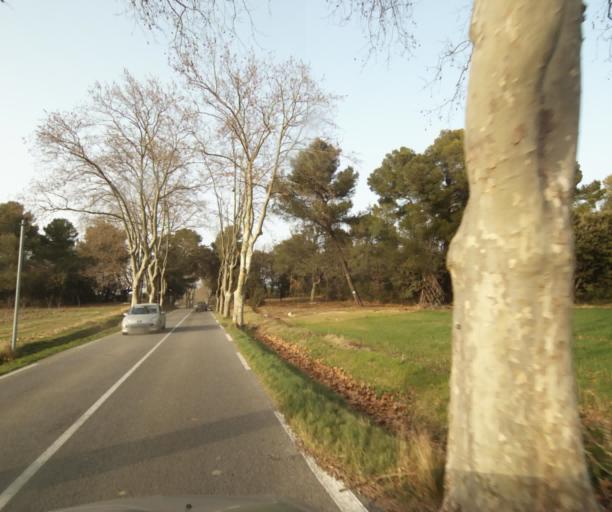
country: FR
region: Provence-Alpes-Cote d'Azur
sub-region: Departement des Bouches-du-Rhone
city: Eguilles
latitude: 43.6062
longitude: 5.3657
